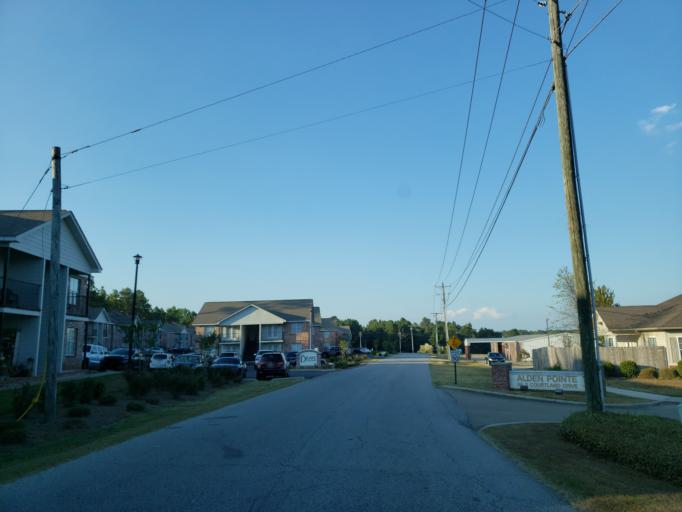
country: US
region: Mississippi
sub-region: Lamar County
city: West Hattiesburg
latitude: 31.3229
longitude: -89.4153
